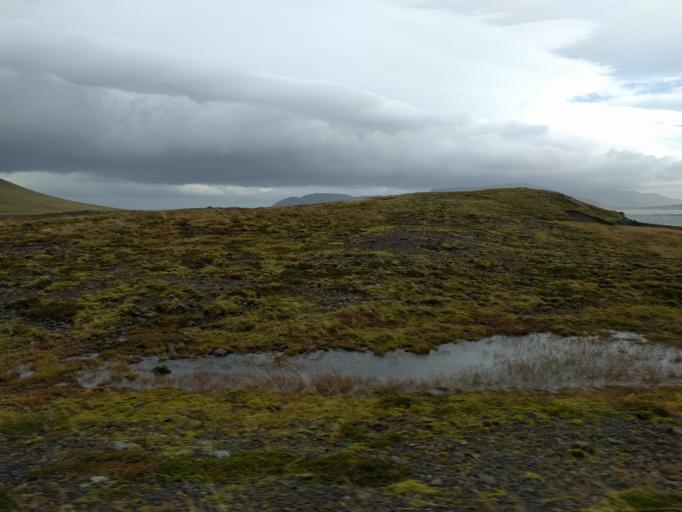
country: IS
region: West
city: Olafsvik
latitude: 64.9250
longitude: -23.3011
